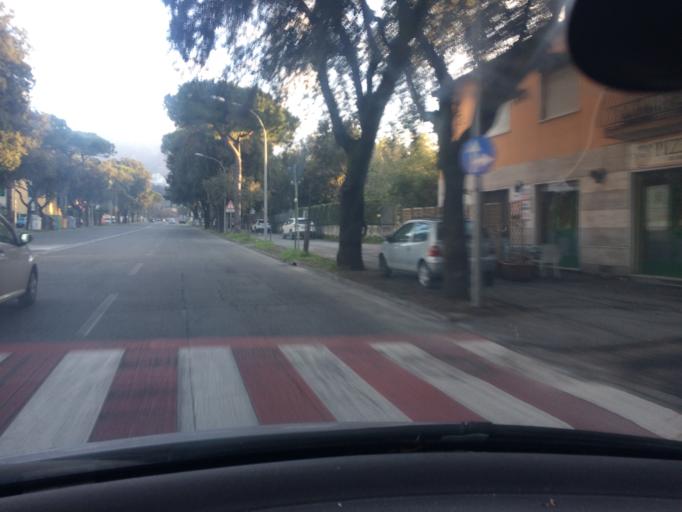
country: IT
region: Tuscany
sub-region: Provincia di Massa-Carrara
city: Carrara
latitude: 44.0580
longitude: 10.0664
